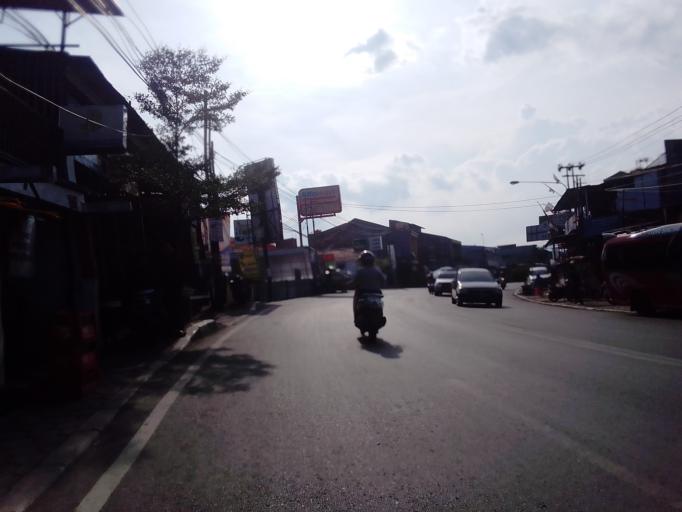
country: ID
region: West Java
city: Cileunyi
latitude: -6.9344
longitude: 107.7168
